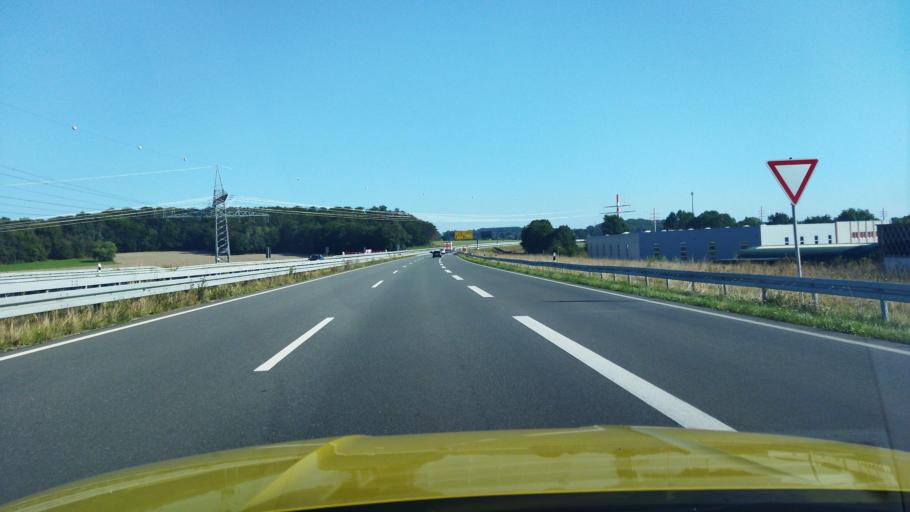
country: DE
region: Lower Saxony
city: Belm
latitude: 52.3008
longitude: 8.1085
